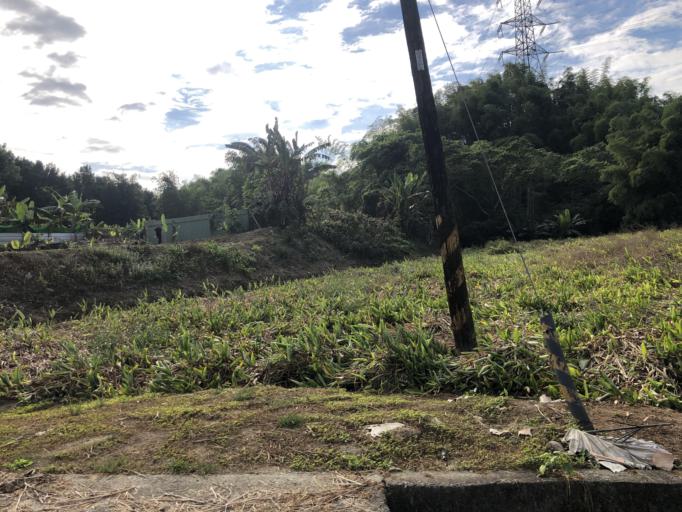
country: TW
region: Taiwan
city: Yujing
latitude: 23.0202
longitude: 120.4143
